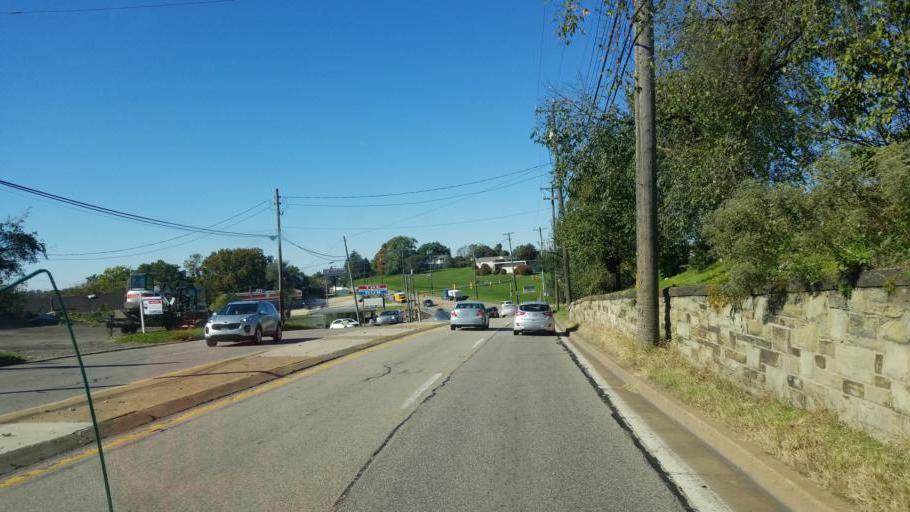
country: US
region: Pennsylvania
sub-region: Allegheny County
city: East McKeesport
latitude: 40.3745
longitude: -79.7956
